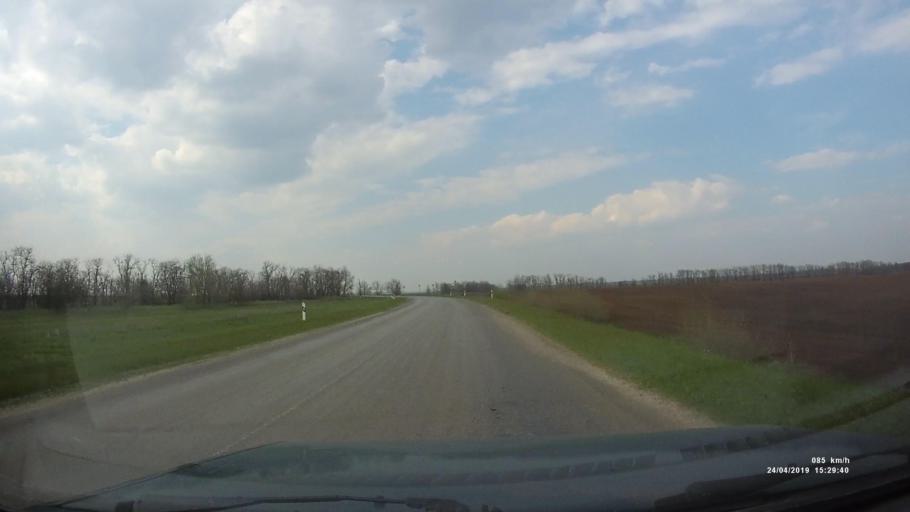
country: RU
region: Rostov
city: Remontnoye
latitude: 46.5955
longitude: 43.0165
